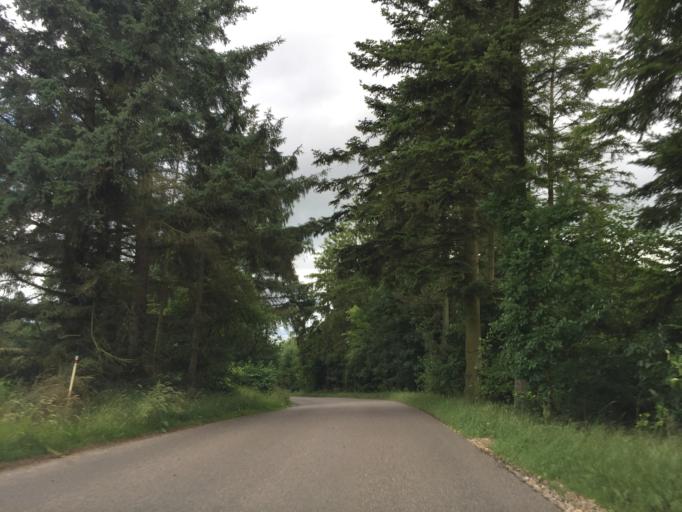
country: DK
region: Central Jutland
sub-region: Silkeborg Kommune
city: Svejbaek
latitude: 56.1728
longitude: 9.6520
